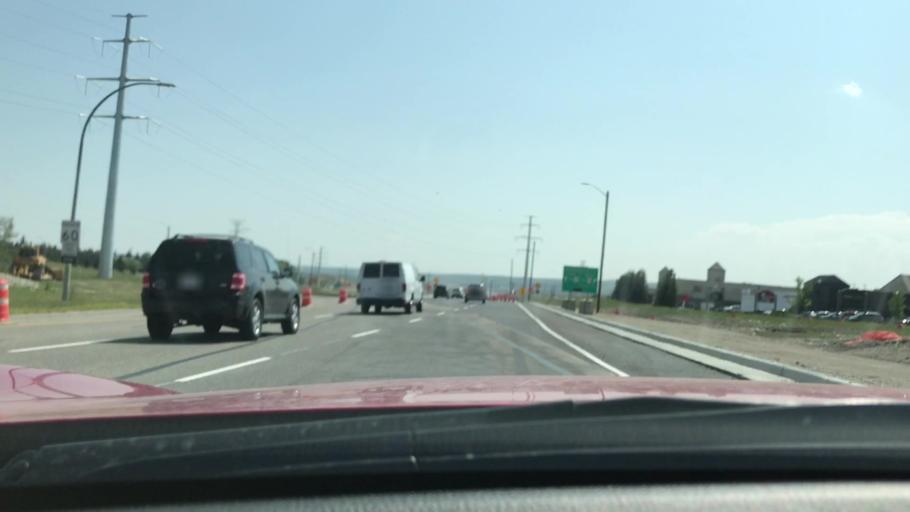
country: CA
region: Alberta
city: Calgary
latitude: 51.0173
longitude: -114.1662
